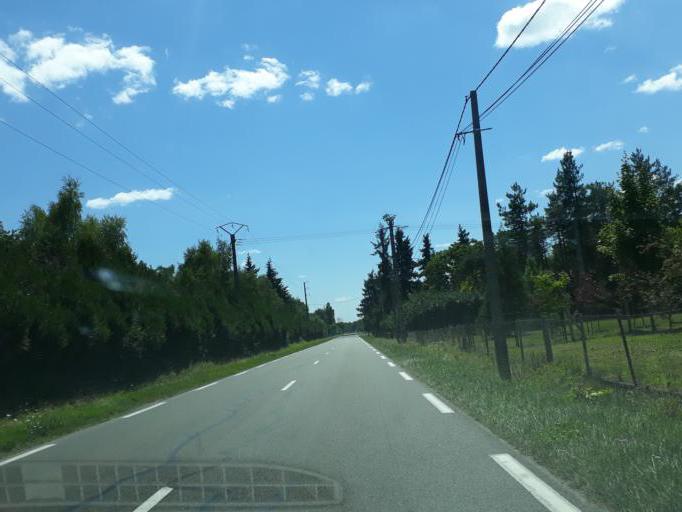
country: FR
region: Centre
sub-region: Departement du Loiret
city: Bray-en-Val
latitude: 47.8087
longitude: 2.3808
